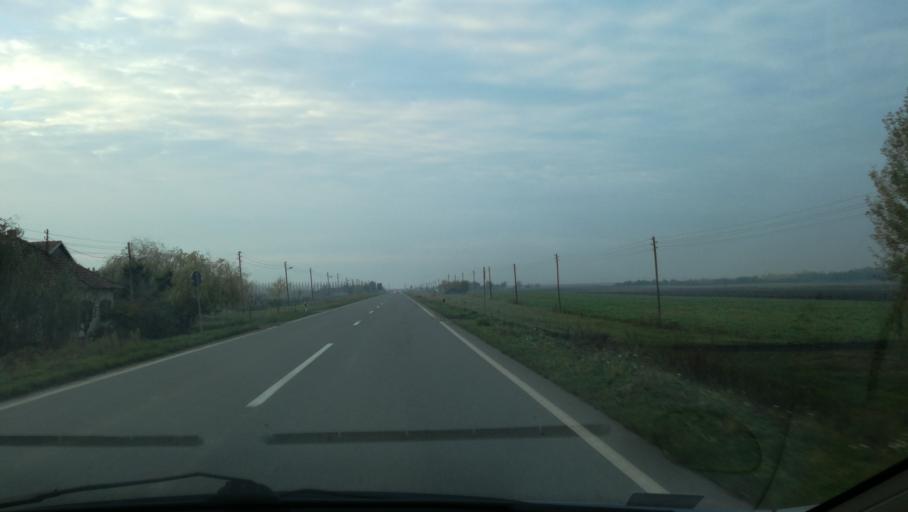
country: RS
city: Basaid
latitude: 45.6835
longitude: 20.4233
